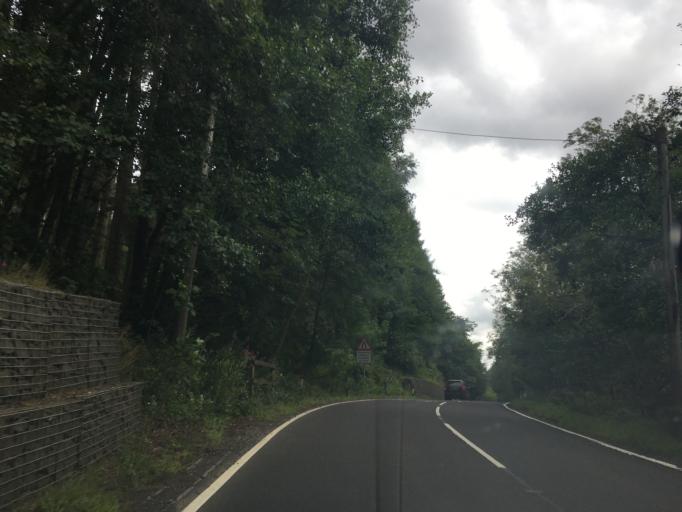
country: GB
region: Scotland
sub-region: Stirling
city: Callander
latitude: 56.3043
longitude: -4.3189
